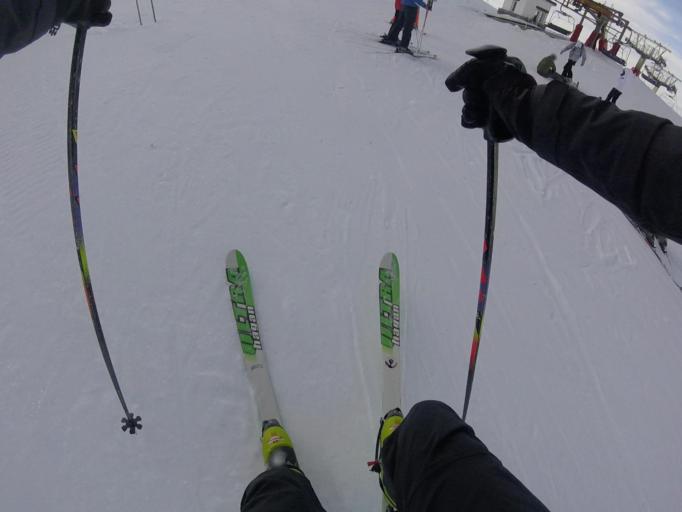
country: ES
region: Andalusia
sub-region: Provincia de Granada
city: Capileira
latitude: 37.0648
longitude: -3.3859
